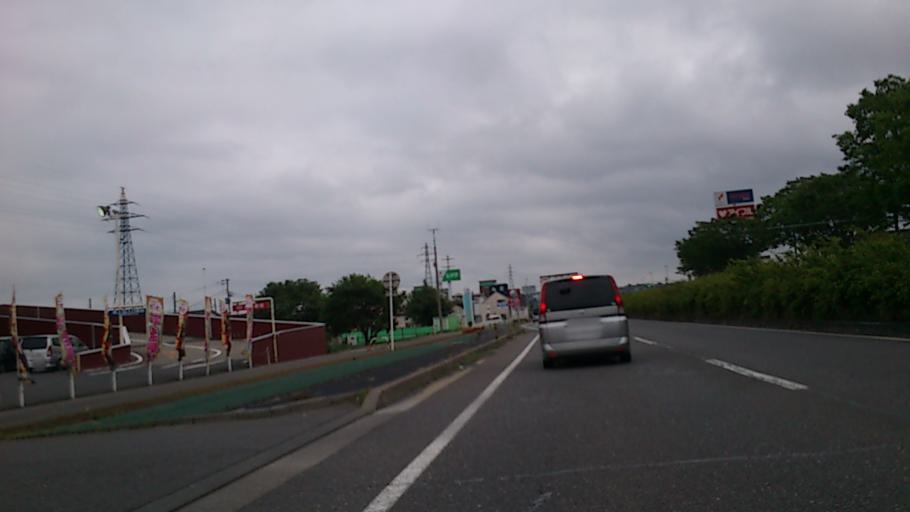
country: JP
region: Fukushima
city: Koriyama
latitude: 37.3743
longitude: 140.3485
